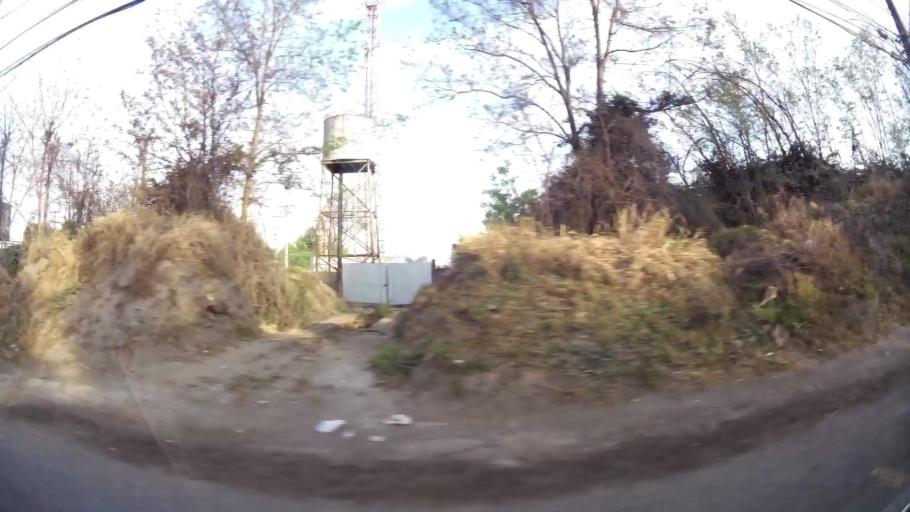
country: CL
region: Santiago Metropolitan
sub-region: Provincia de Maipo
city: San Bernardo
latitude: -33.5440
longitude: -70.7434
